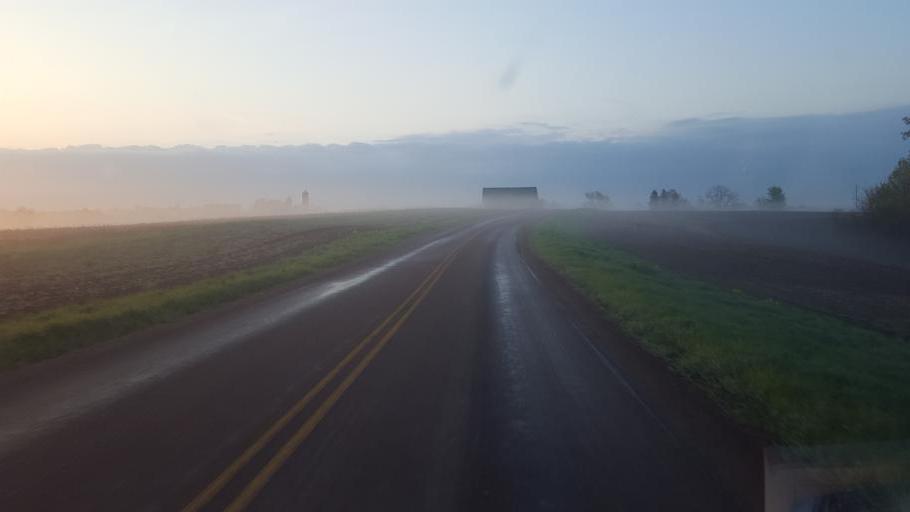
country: US
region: Wisconsin
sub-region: Vernon County
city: Hillsboro
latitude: 43.5998
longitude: -90.4190
